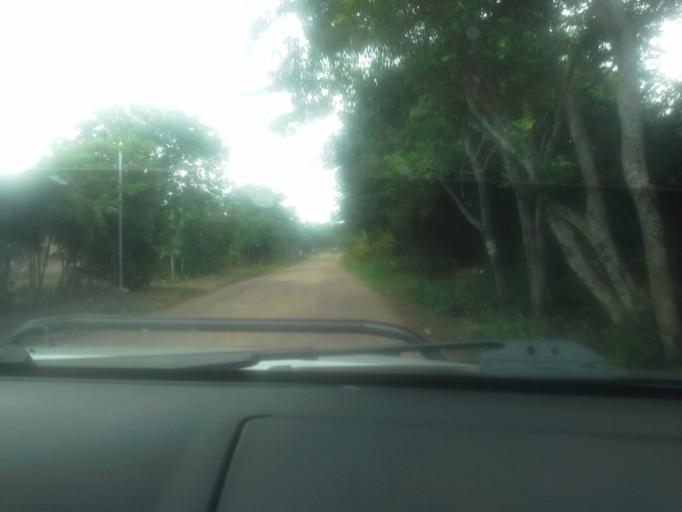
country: NI
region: Matagalpa
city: Ciudad Dario
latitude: 12.8194
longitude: -86.1930
